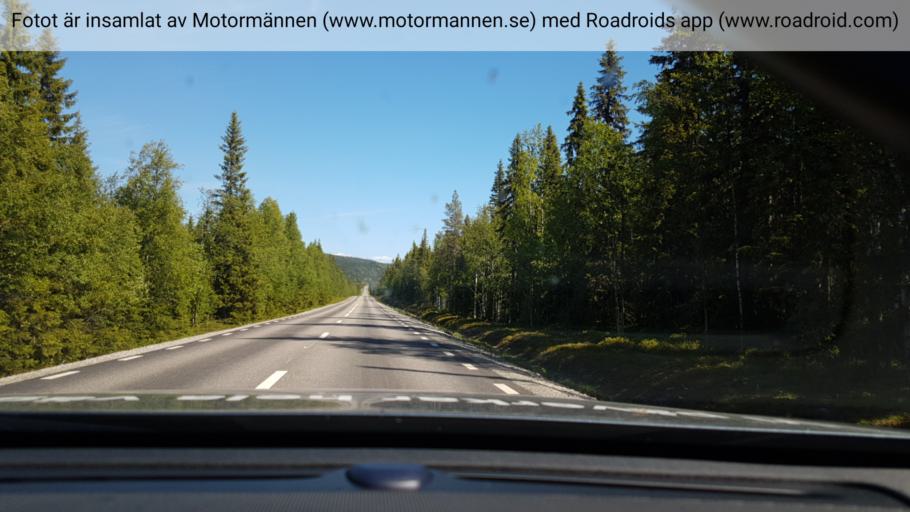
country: SE
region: Vaesterbotten
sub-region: Asele Kommun
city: Insjon
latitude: 64.7236
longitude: 17.6136
